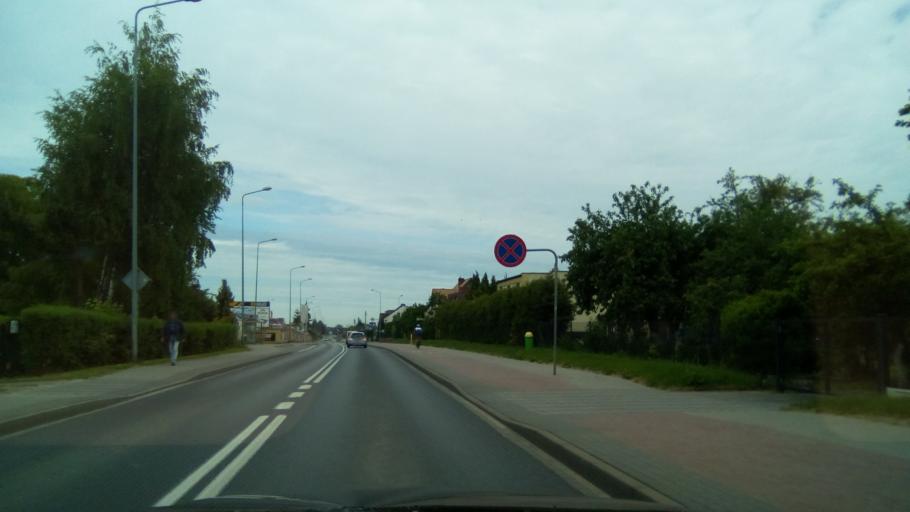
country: PL
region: Pomeranian Voivodeship
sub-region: Powiat chojnicki
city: Chojnice
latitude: 53.7042
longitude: 17.5482
